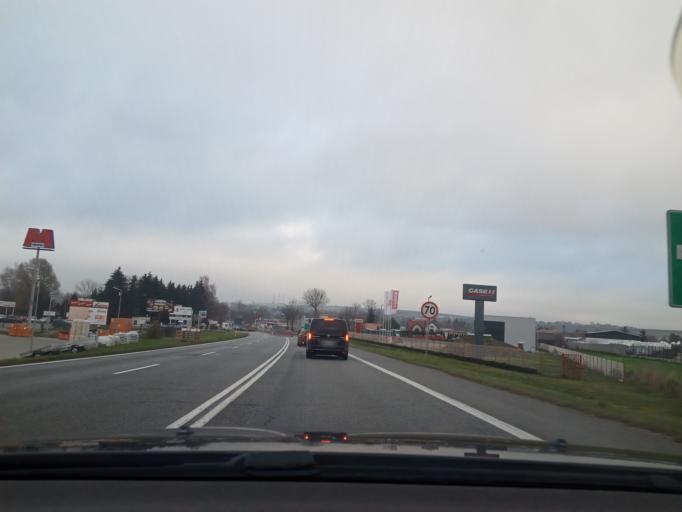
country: PL
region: Lesser Poland Voivodeship
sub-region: Powiat miechowski
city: Miechow
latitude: 50.3544
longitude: 20.0442
